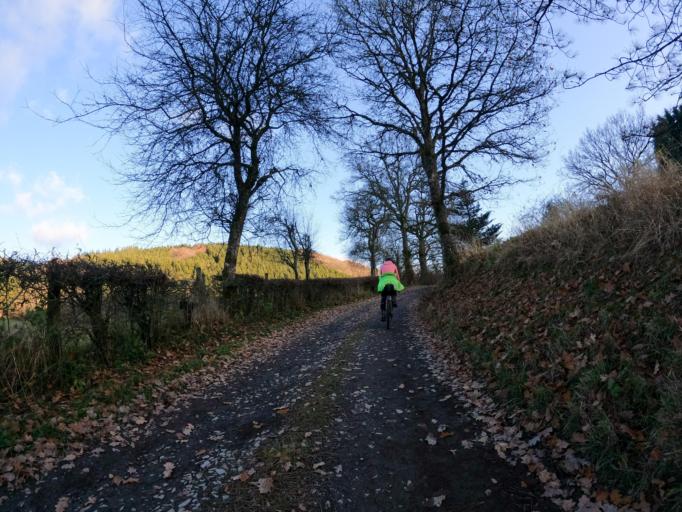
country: LU
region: Diekirch
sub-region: Canton de Wiltz
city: Bavigne
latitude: 49.9608
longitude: 5.8275
